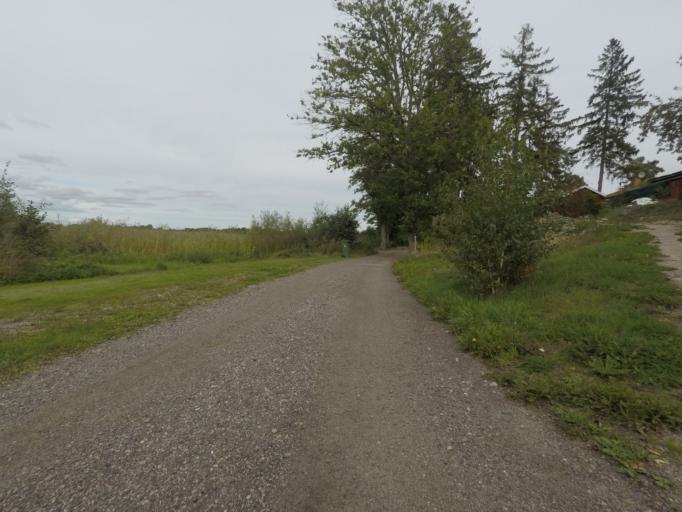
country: SE
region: Vaestmanland
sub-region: Kungsors Kommun
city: Kungsoer
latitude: 59.4656
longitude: 16.0707
